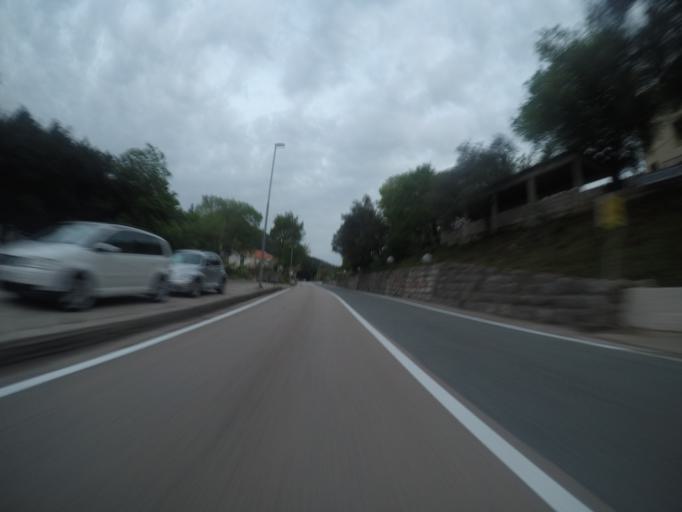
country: ME
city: Petrovac na Moru
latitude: 42.1994
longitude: 18.9666
